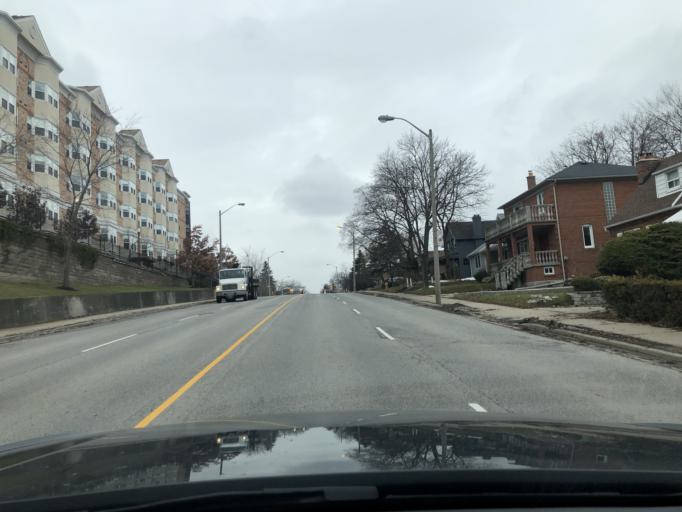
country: CA
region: Ontario
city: Etobicoke
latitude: 43.6978
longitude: -79.5253
